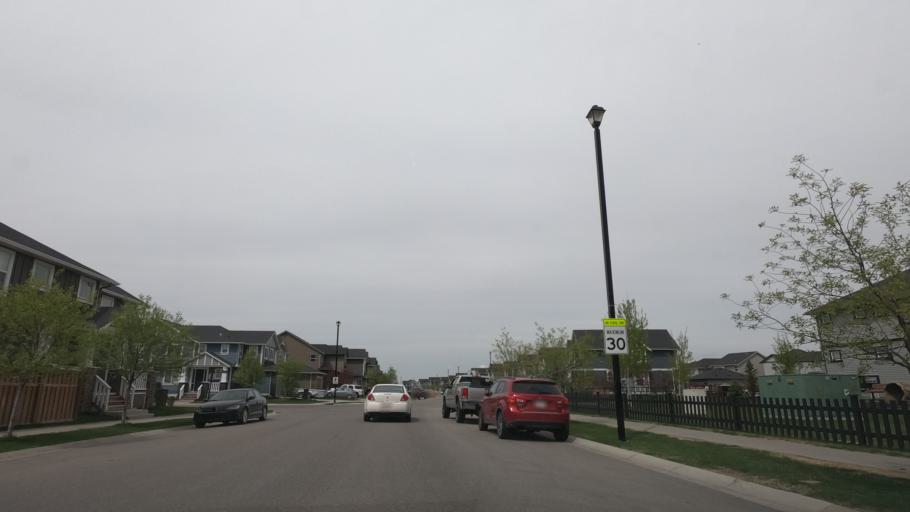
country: CA
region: Alberta
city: Airdrie
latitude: 51.3043
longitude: -114.0338
